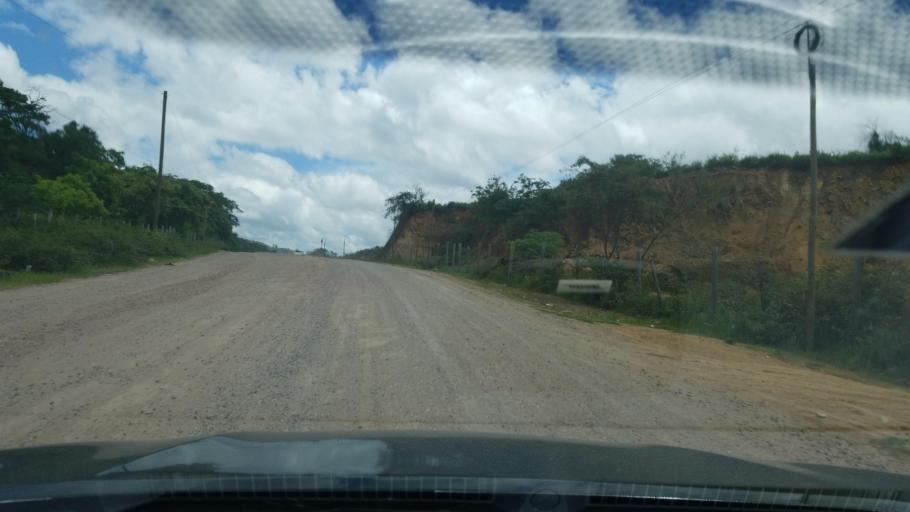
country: HN
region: Francisco Morazan
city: Talanga
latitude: 14.3850
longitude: -87.0708
